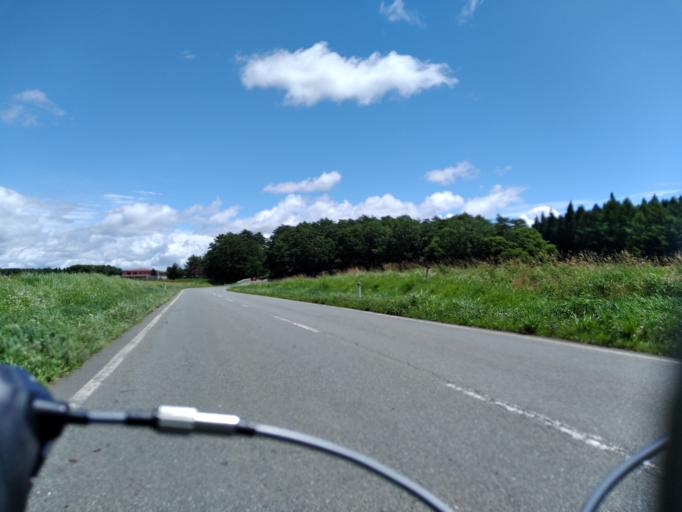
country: JP
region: Iwate
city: Shizukuishi
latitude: 39.7559
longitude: 141.0083
